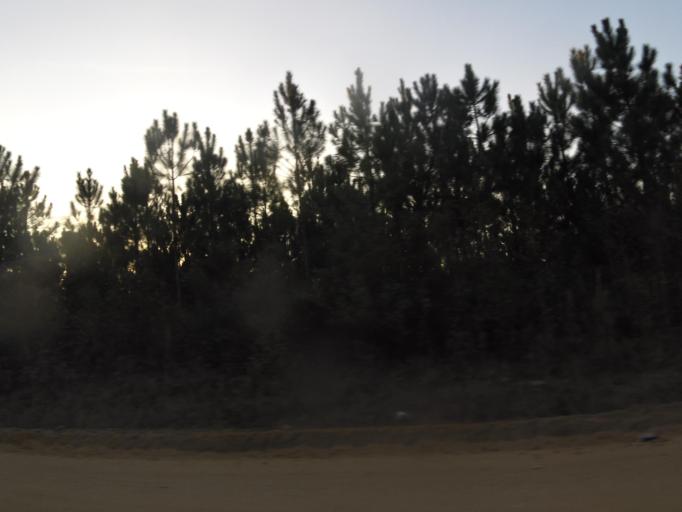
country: US
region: Florida
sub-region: Clay County
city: Green Cove Springs
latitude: 29.8888
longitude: -81.7895
